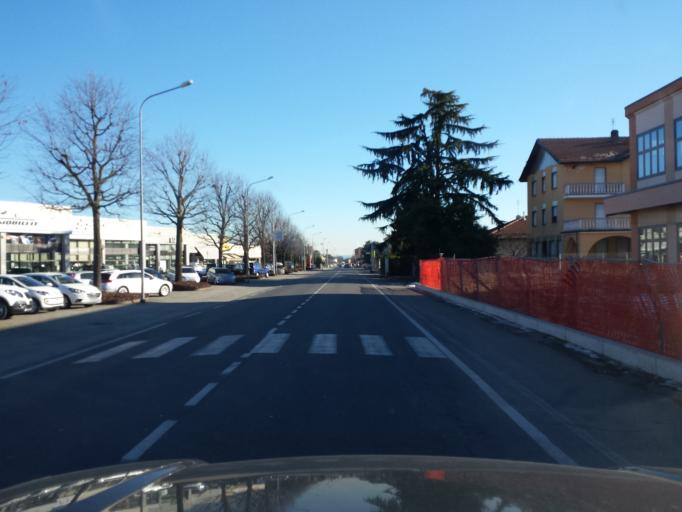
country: IT
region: Piedmont
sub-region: Provincia di Torino
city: Feletto
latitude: 45.3145
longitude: 7.7370
